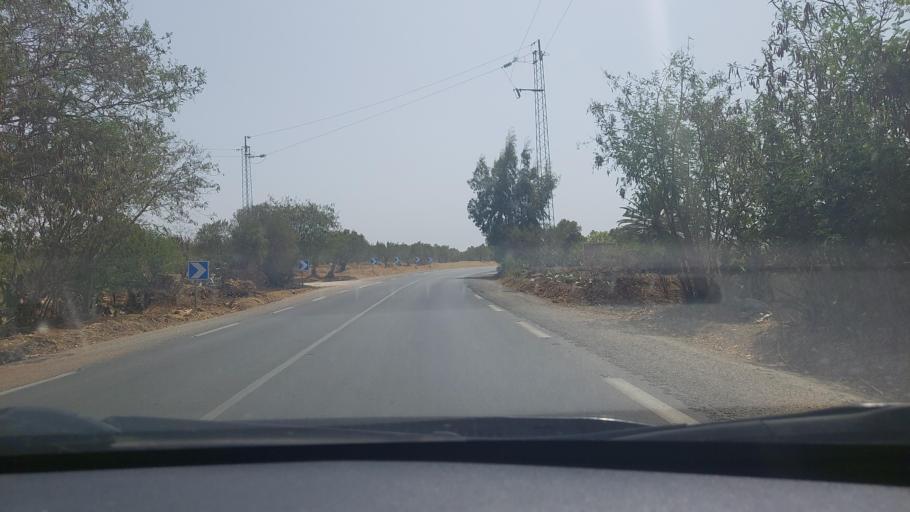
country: TN
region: Al Munastir
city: Sidi Bin Nur
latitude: 35.5735
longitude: 10.9101
